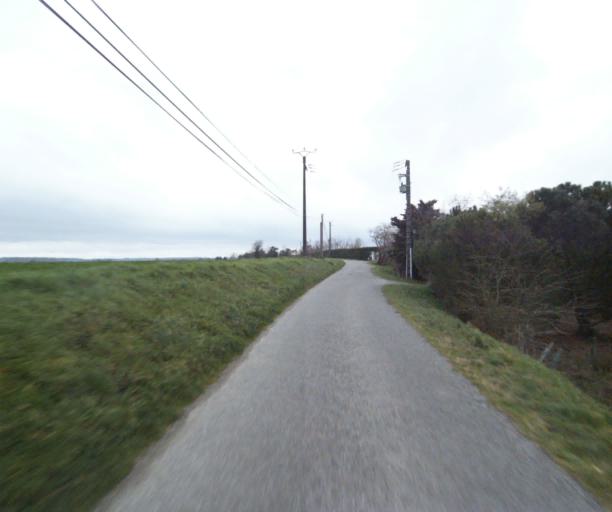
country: FR
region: Midi-Pyrenees
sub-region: Departement de l'Ariege
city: Saverdun
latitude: 43.2414
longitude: 1.5916
